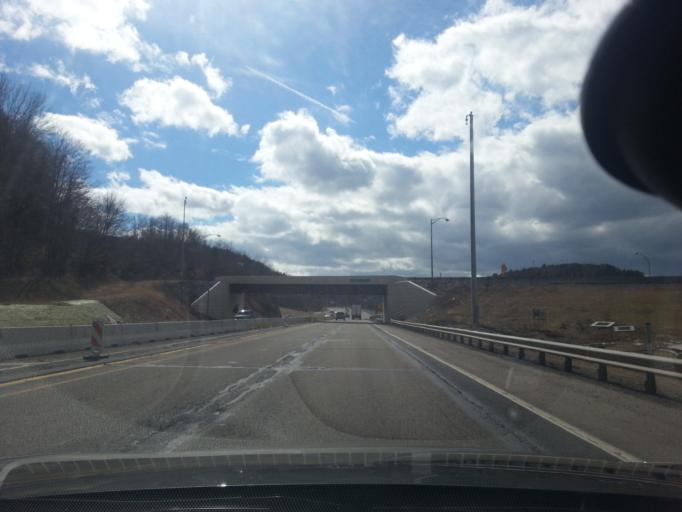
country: US
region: Pennsylvania
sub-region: Carbon County
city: Weissport East
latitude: 40.8363
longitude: -75.6716
